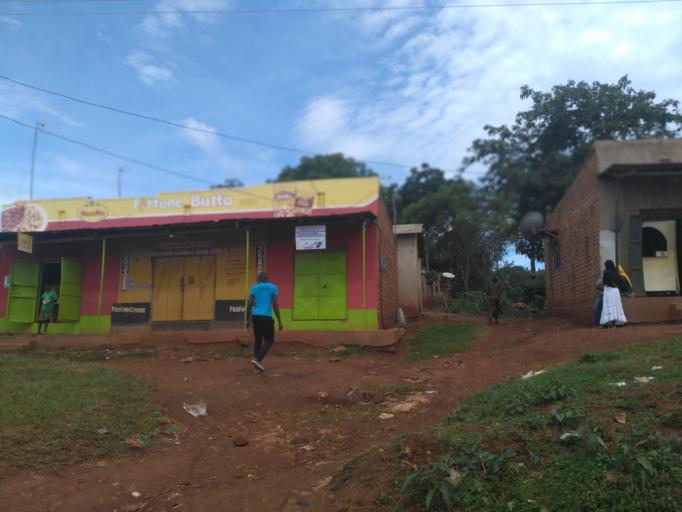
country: UG
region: Central Region
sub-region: Buikwe District
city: Njeru
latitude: 0.4033
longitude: 33.1774
